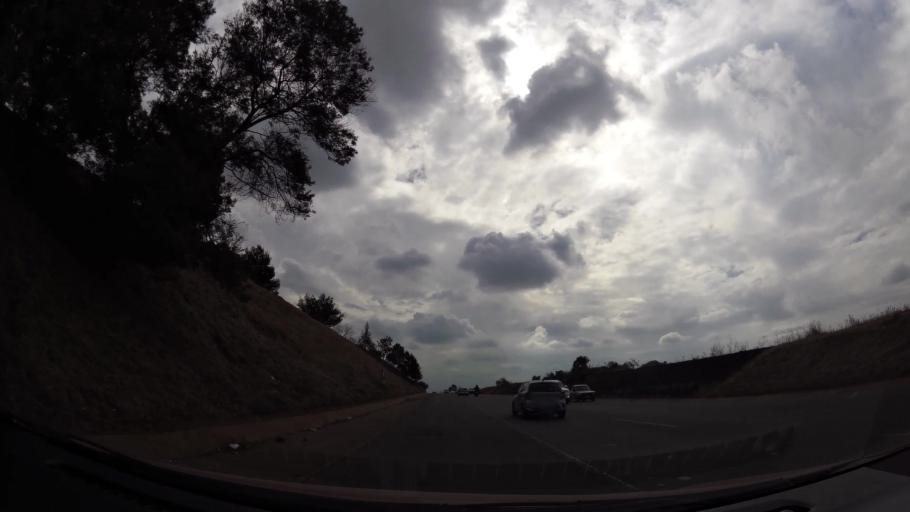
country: ZA
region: Gauteng
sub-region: City of Johannesburg Metropolitan Municipality
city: Roodepoort
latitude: -26.1044
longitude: 27.8803
